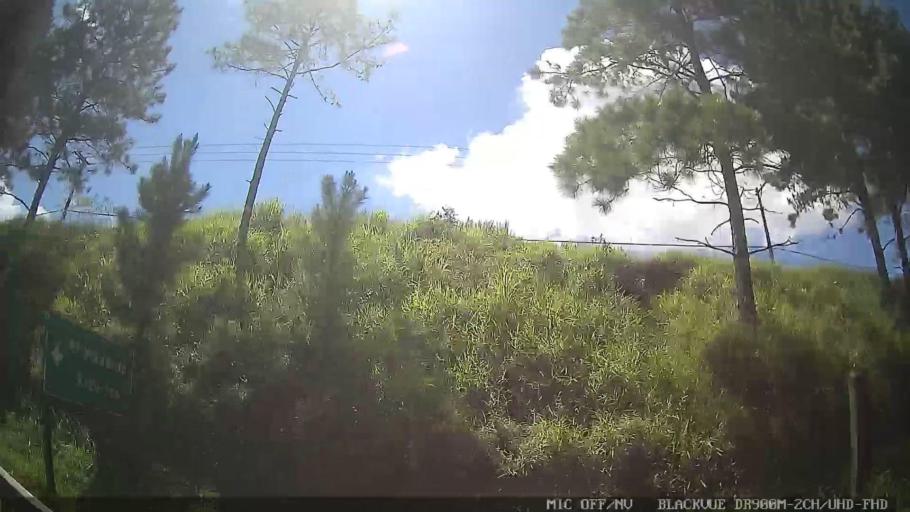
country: BR
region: Sao Paulo
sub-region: Mogi das Cruzes
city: Mogi das Cruzes
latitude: -23.6594
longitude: -46.2037
